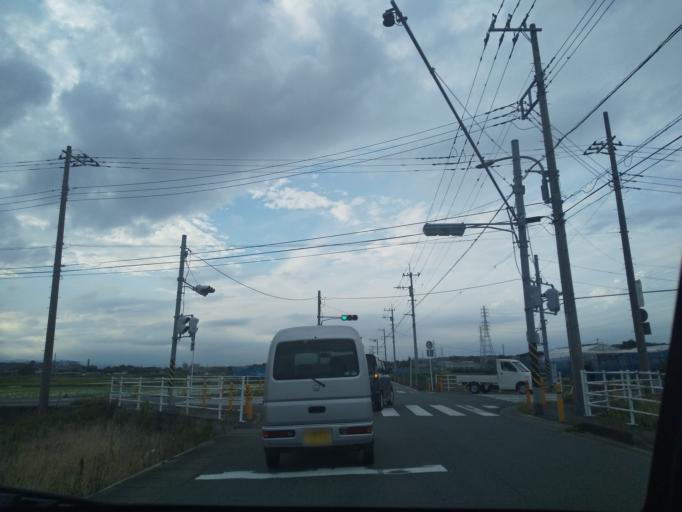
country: JP
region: Kanagawa
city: Zama
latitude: 35.4900
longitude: 139.3850
